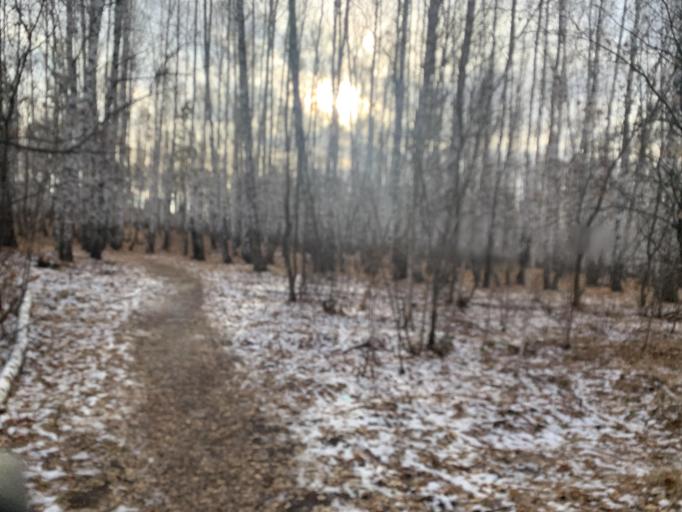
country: RU
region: Chelyabinsk
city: Roshchino
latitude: 55.2021
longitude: 61.3031
